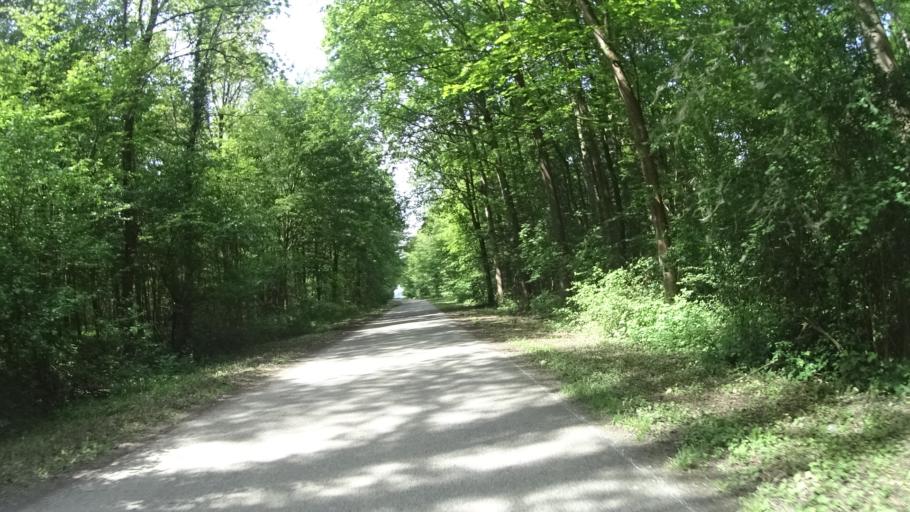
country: DE
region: Baden-Wuerttemberg
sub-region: Freiburg Region
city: Meissenheim
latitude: 48.4304
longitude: 7.7956
